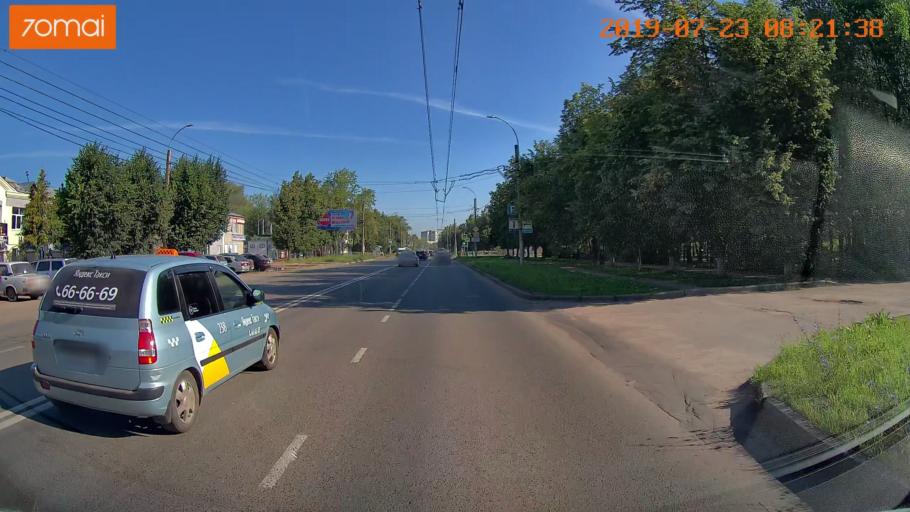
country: RU
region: Ivanovo
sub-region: Gorod Ivanovo
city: Ivanovo
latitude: 56.9757
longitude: 40.9657
